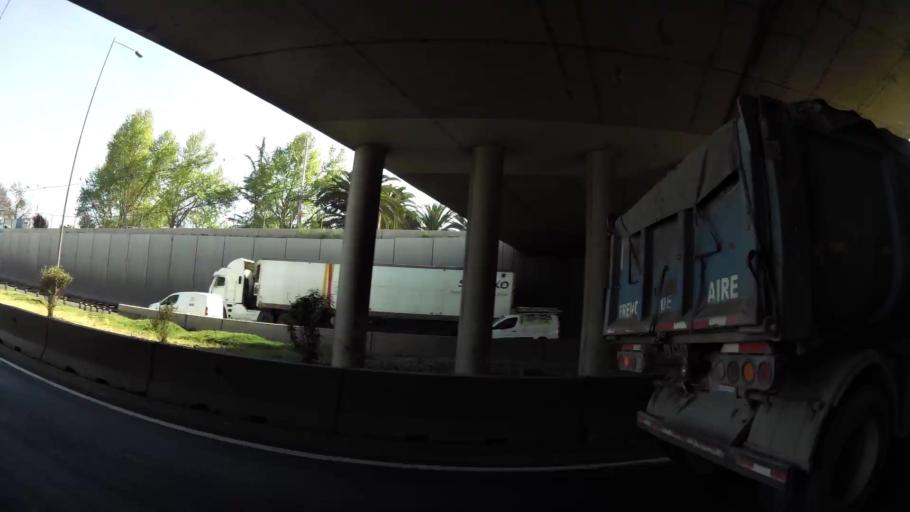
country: CL
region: Santiago Metropolitan
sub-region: Provincia de Santiago
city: Lo Prado
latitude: -33.4632
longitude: -70.7634
